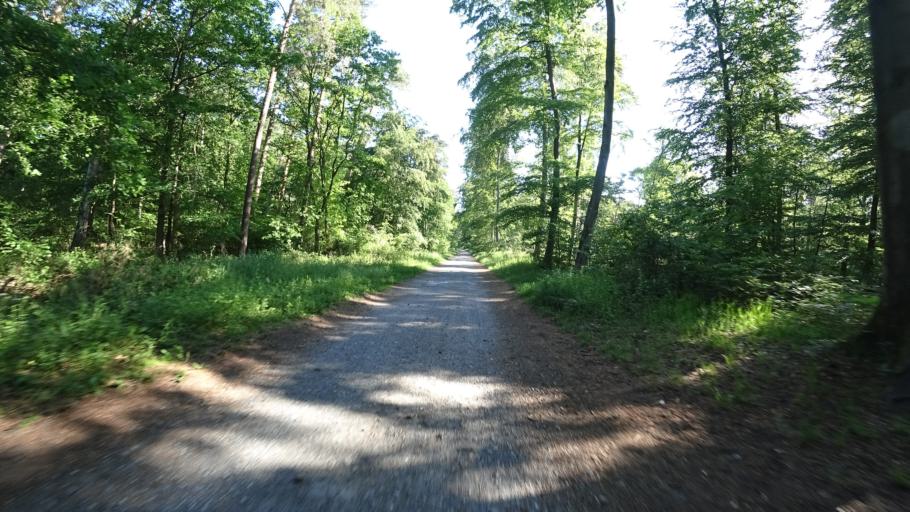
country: DE
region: North Rhine-Westphalia
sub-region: Regierungsbezirk Detmold
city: Rheda-Wiedenbruck
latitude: 51.8914
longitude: 8.3213
